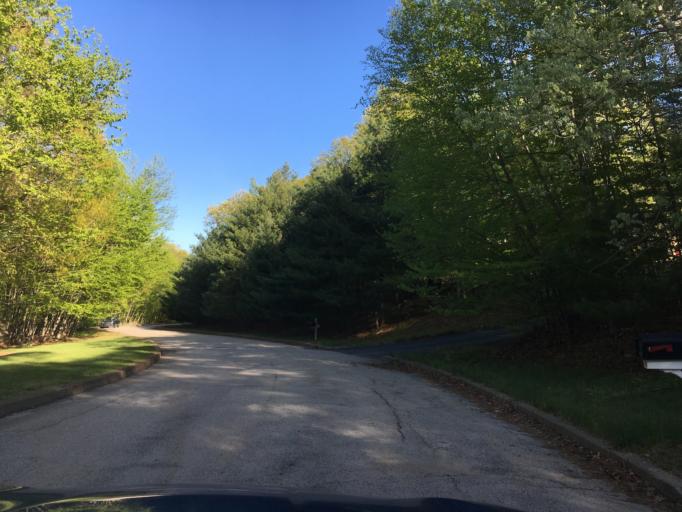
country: US
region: Rhode Island
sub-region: Washington County
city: Exeter
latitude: 41.6117
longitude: -71.5228
